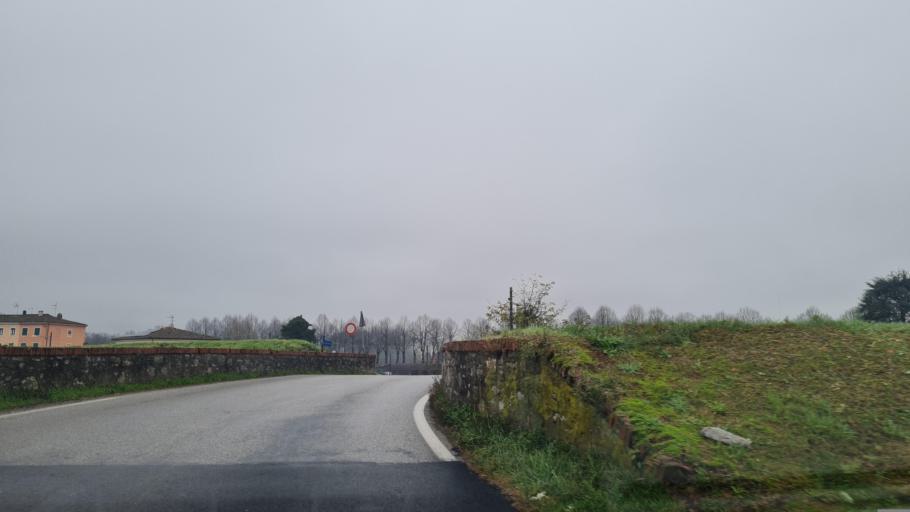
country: IT
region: Tuscany
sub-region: Provincia di Lucca
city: Lucca
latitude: 43.8562
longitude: 10.4472
